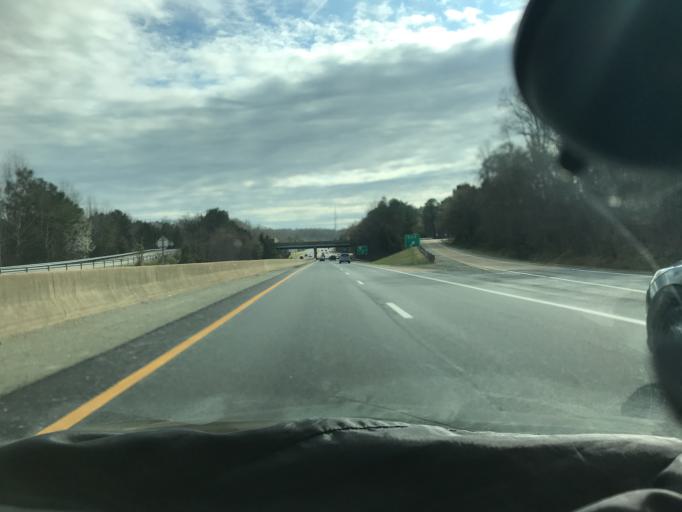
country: US
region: Virginia
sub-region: Chesterfield County
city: Bon Air
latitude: 37.5211
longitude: -77.5335
